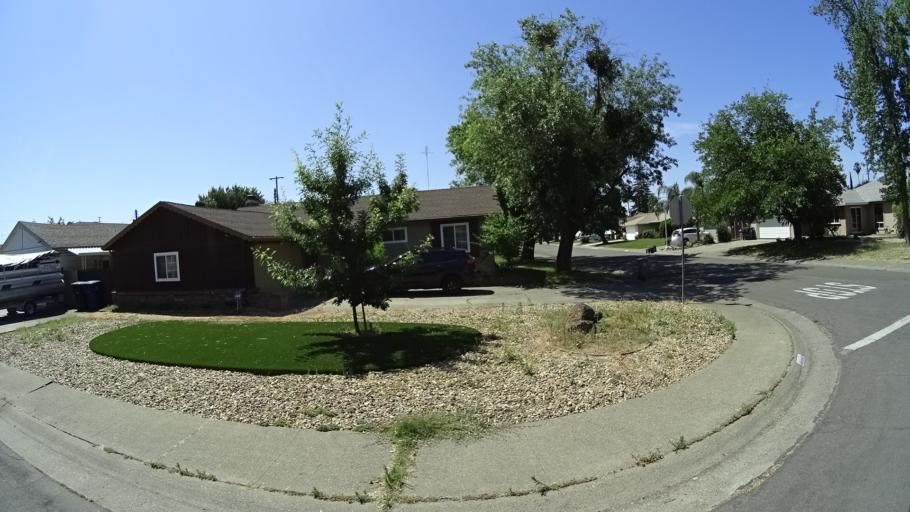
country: US
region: California
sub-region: Sacramento County
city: Florin
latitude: 38.5300
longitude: -121.4113
